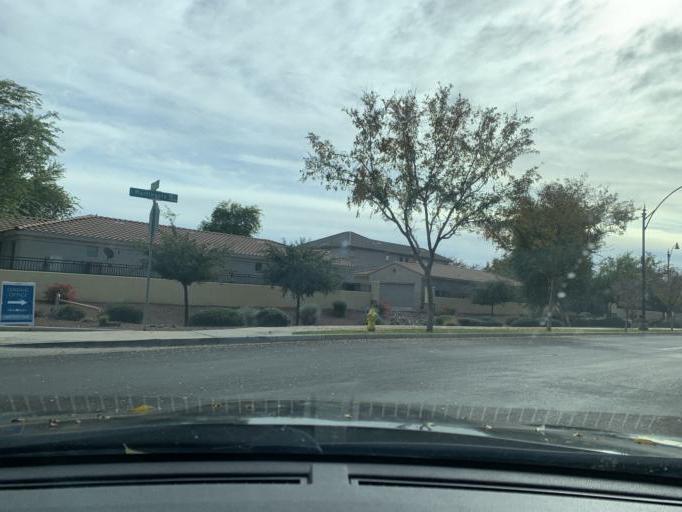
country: US
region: Arizona
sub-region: Maricopa County
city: Gilbert
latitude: 33.3243
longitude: -111.7170
